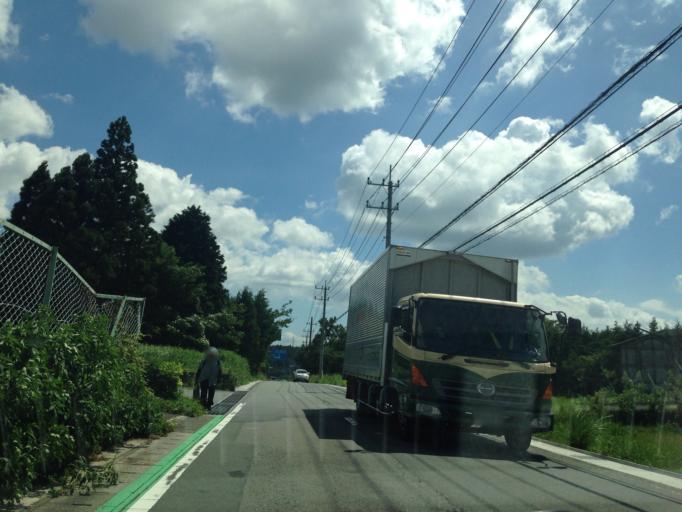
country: JP
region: Shizuoka
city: Gotemba
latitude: 35.2322
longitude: 138.8777
